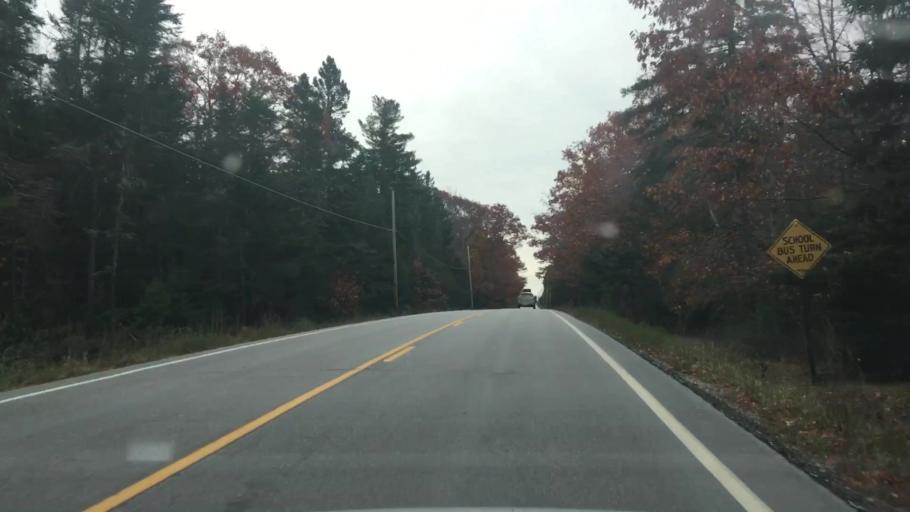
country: US
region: Maine
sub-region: Hancock County
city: Penobscot
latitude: 44.4914
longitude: -68.6437
